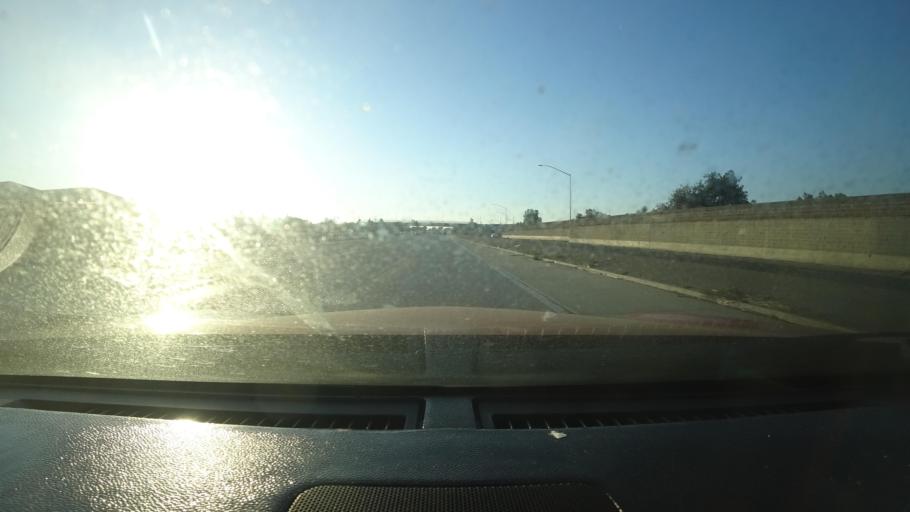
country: US
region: California
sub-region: Santa Clara County
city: San Jose
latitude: 37.3520
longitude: -121.8634
